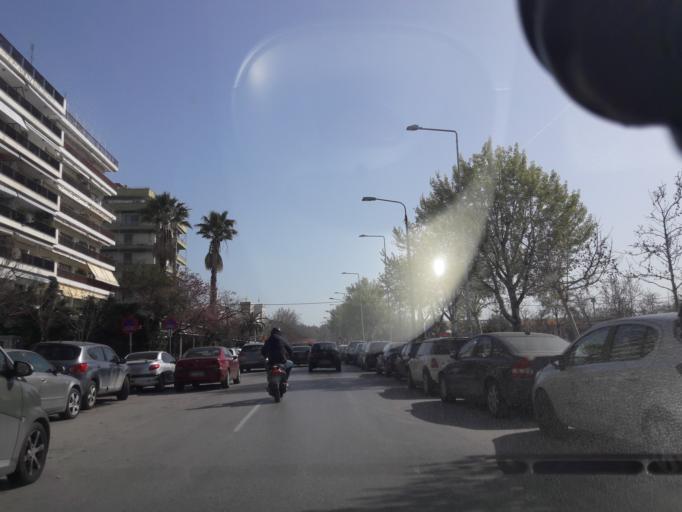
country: GR
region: Central Macedonia
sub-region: Nomos Thessalonikis
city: Kalamaria
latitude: 40.6000
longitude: 22.9498
